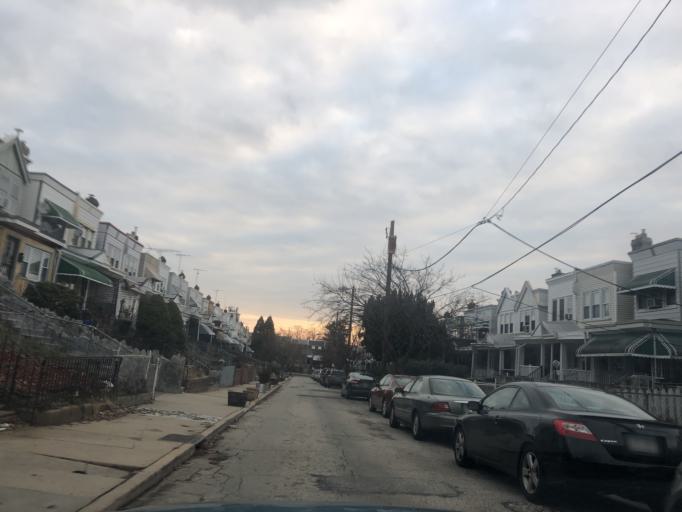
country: US
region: Pennsylvania
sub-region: Delaware County
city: Millbourne
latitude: 39.9786
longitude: -75.2376
